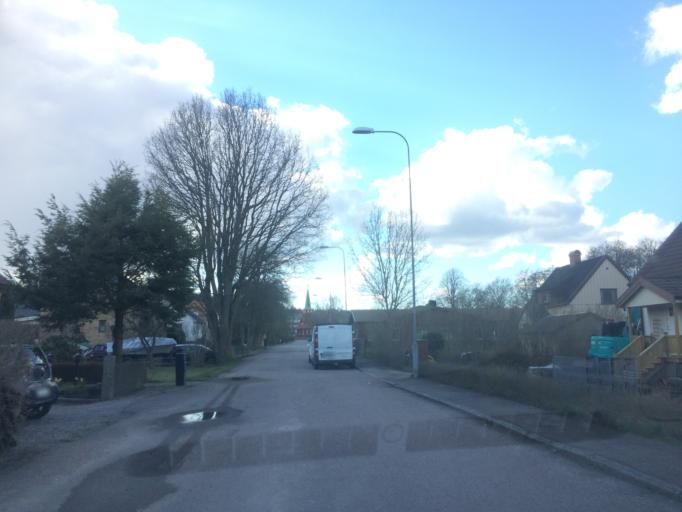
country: SE
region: Vaestra Goetaland
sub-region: Goteborg
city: Gardsten
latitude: 57.7901
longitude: 11.9950
